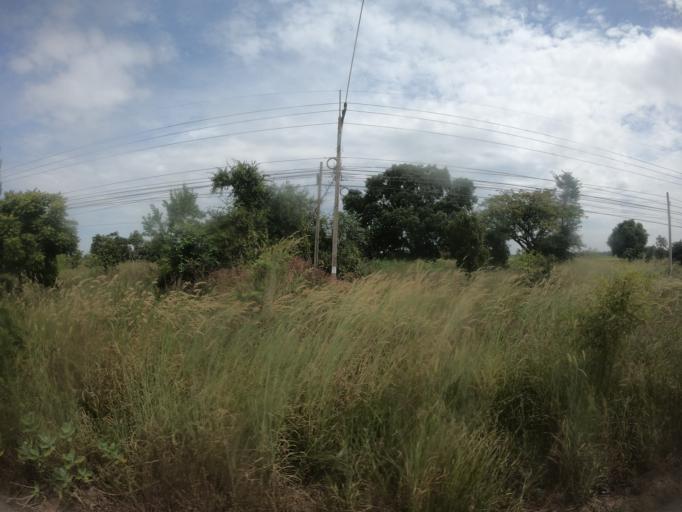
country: TH
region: Maha Sarakham
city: Chiang Yuen
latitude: 16.3593
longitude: 103.1120
